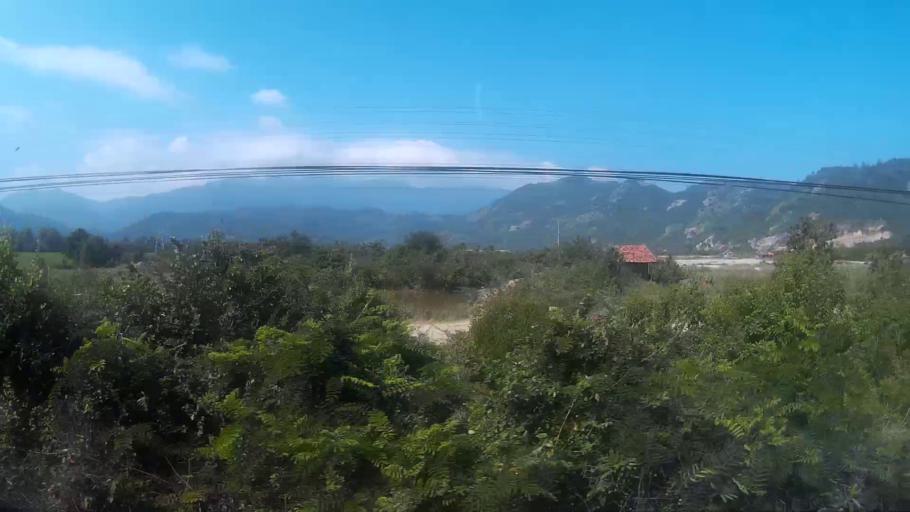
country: VN
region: Khanh Hoa
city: Ninh Hoa
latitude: 12.4064
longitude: 109.1510
